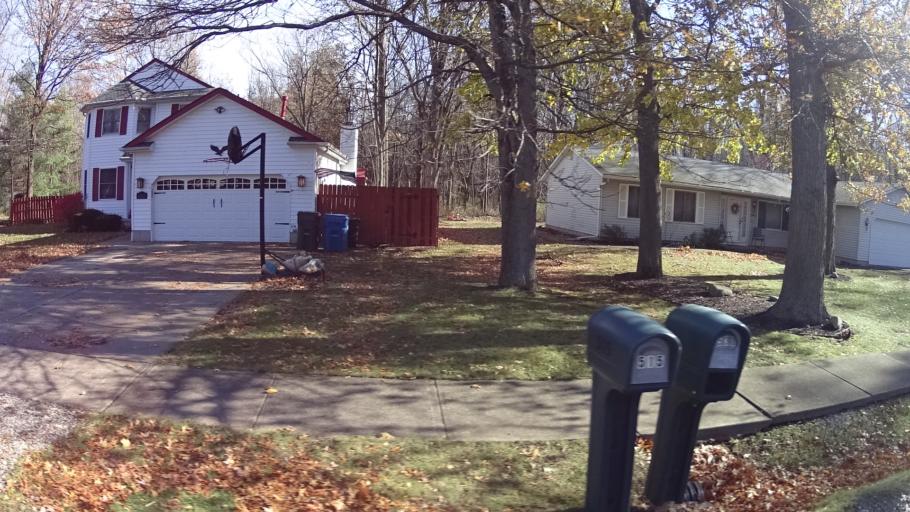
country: US
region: Ohio
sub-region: Lorain County
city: Sheffield Lake
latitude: 41.4913
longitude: -82.0809
